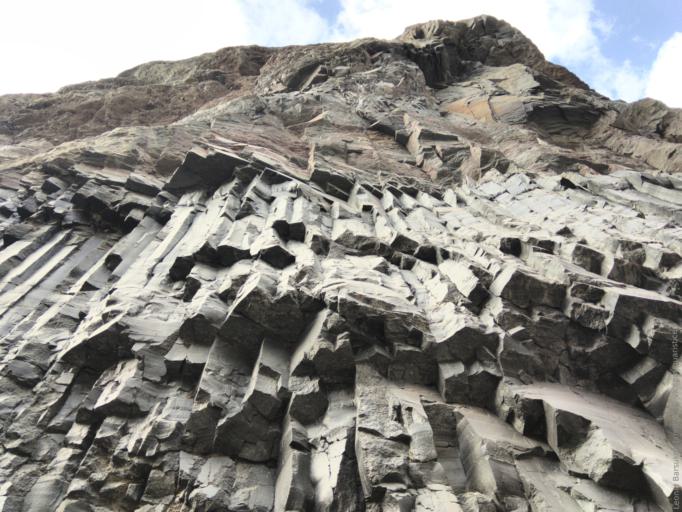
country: RU
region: Kabardino-Balkariya
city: Terskol
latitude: 43.2662
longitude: 42.4646
